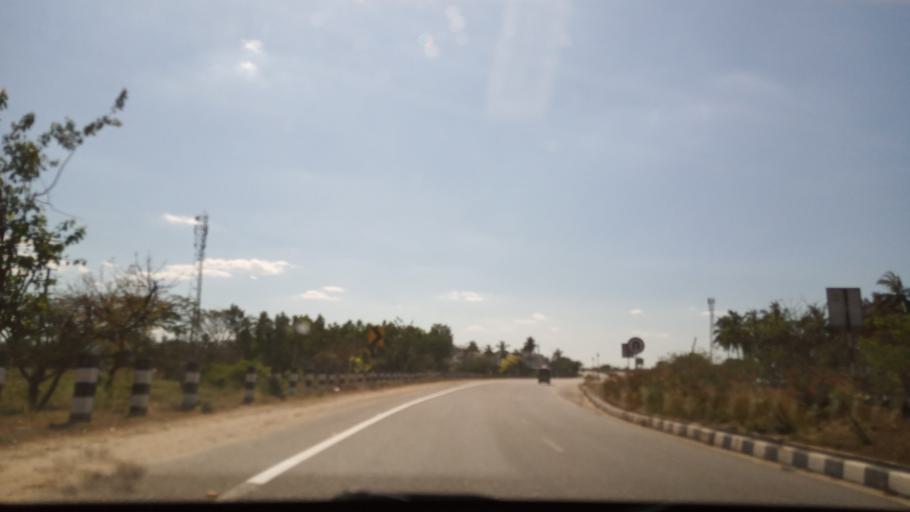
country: IN
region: Karnataka
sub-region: Kolar
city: Mulbagal
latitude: 13.1992
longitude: 78.4822
